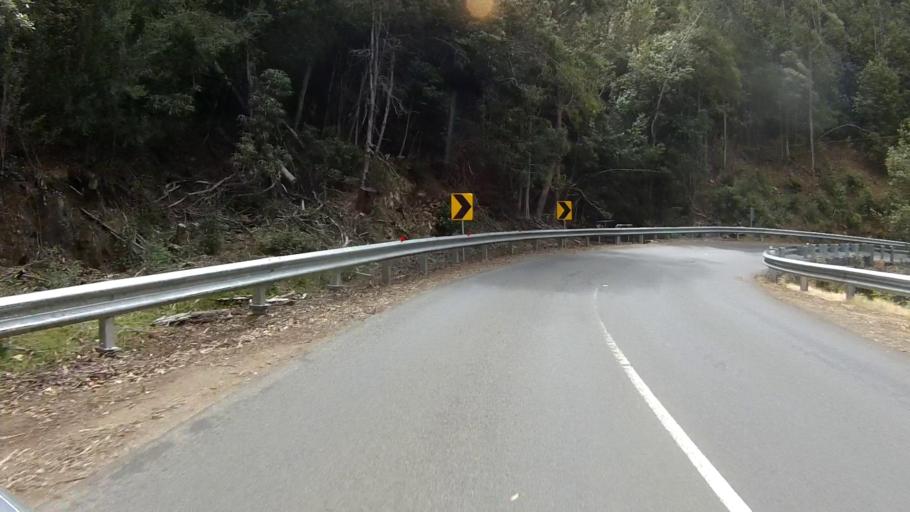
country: AU
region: Tasmania
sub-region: Kingborough
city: Kingston
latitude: -42.9407
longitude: 147.2400
